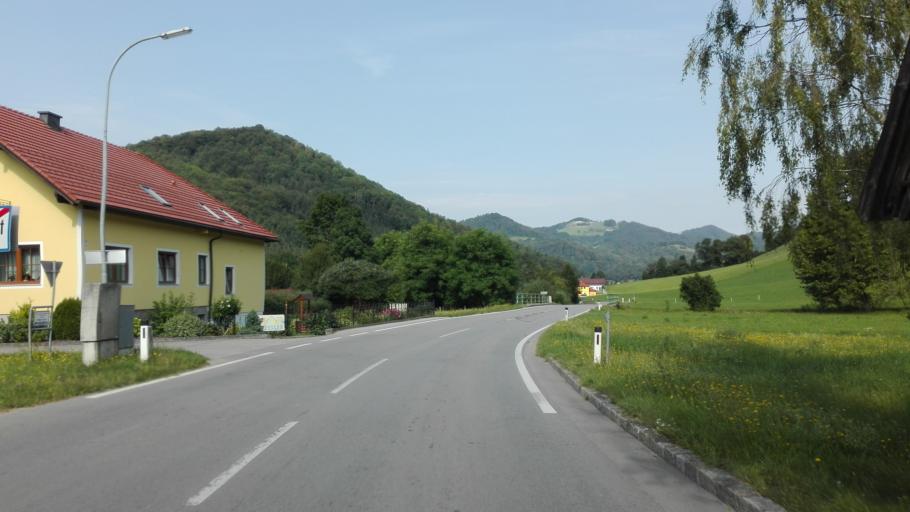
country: AT
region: Lower Austria
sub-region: Politischer Bezirk Sankt Polten
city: Rabenstein an der Pielach
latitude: 48.0317
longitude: 15.4676
